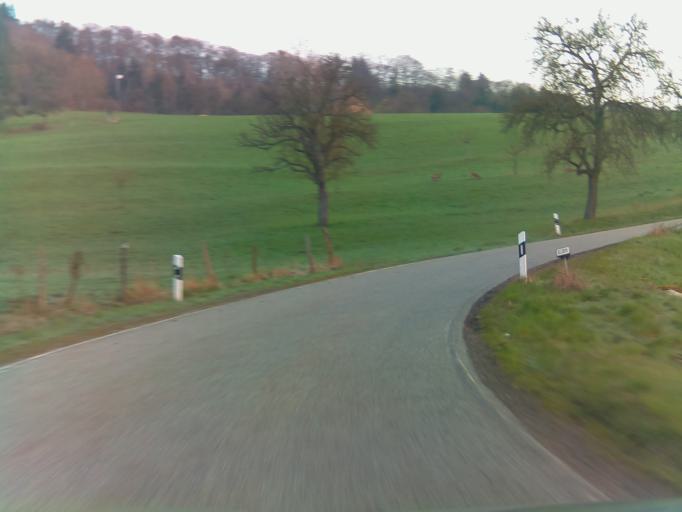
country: DE
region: Rheinland-Pfalz
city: Kirrweiler
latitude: 49.6305
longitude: 7.4978
